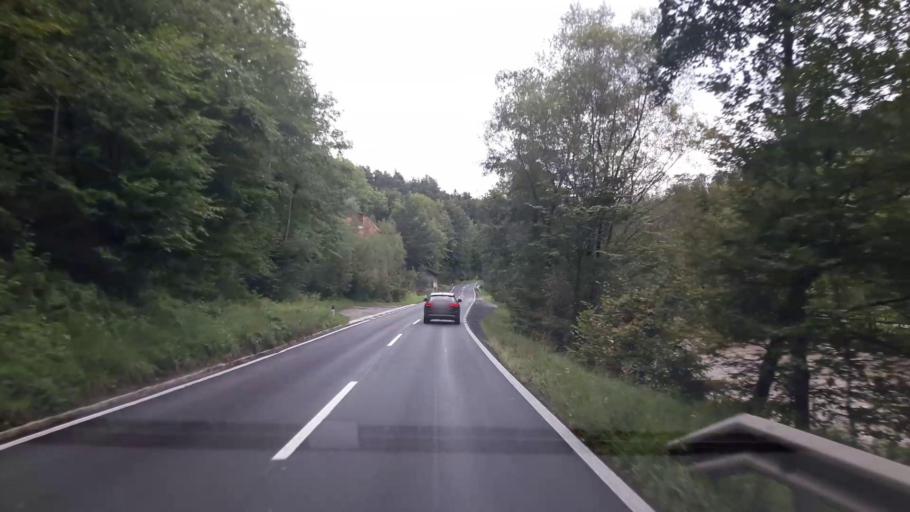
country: AT
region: Styria
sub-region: Politischer Bezirk Hartberg-Fuerstenfeld
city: Stubenberg
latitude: 47.2434
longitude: 15.7873
